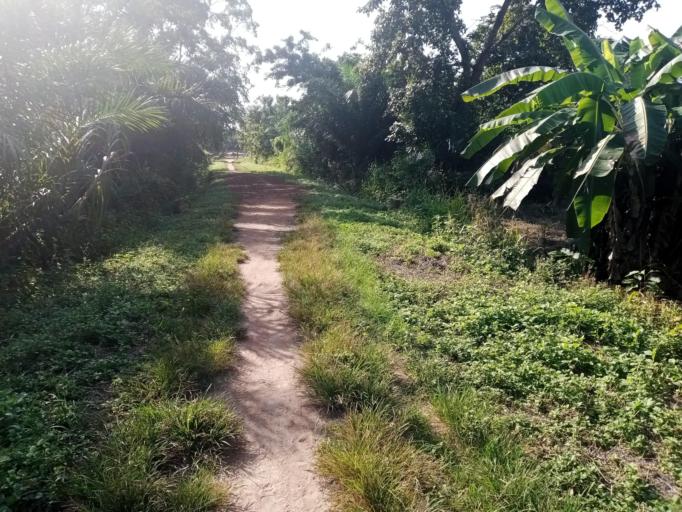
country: TG
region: Maritime
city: Tsevie
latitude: 6.6551
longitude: 0.9732
